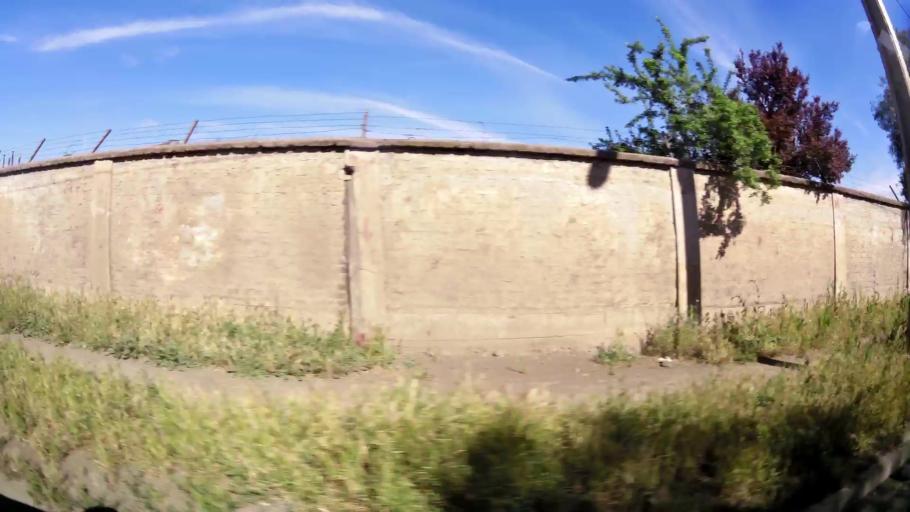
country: CL
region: Santiago Metropolitan
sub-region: Provincia de Santiago
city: Lo Prado
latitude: -33.4850
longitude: -70.7103
